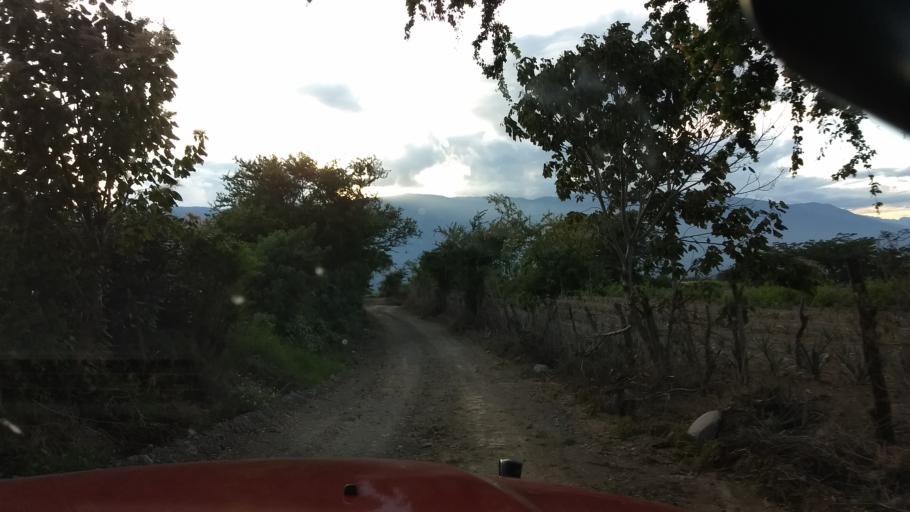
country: MX
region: Colima
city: Suchitlan
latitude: 19.4963
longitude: -103.7730
